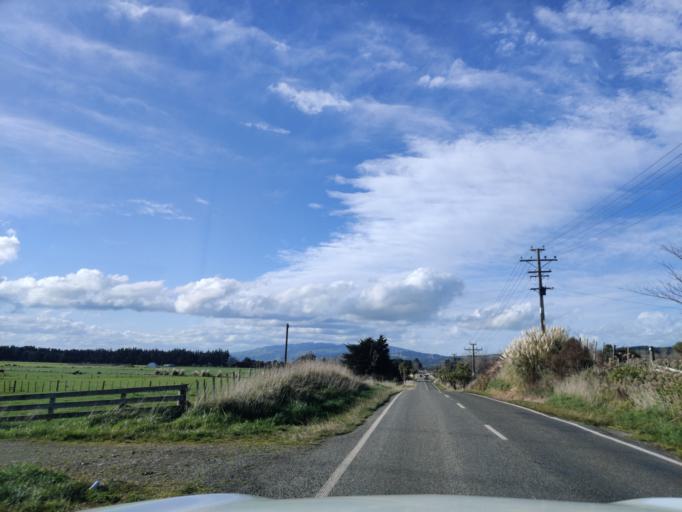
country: NZ
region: Manawatu-Wanganui
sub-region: Palmerston North City
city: Palmerston North
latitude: -40.3437
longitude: 175.7119
